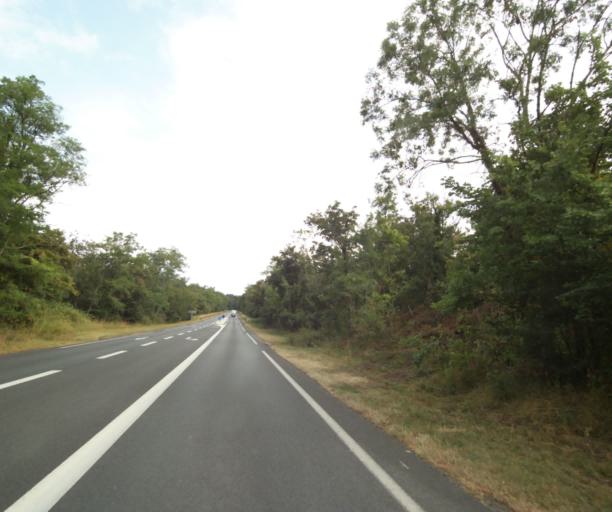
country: FR
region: Ile-de-France
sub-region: Departement de Seine-et-Marne
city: Fontainebleau
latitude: 48.4344
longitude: 2.6963
